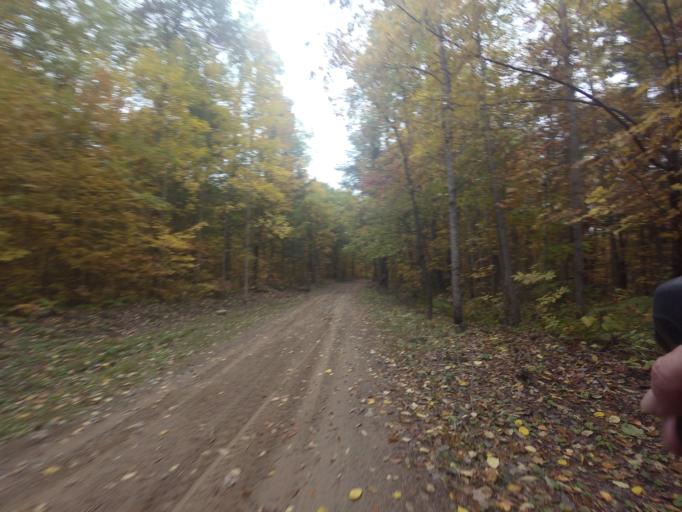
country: CA
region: Ontario
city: Petawawa
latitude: 45.7554
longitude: -77.3621
